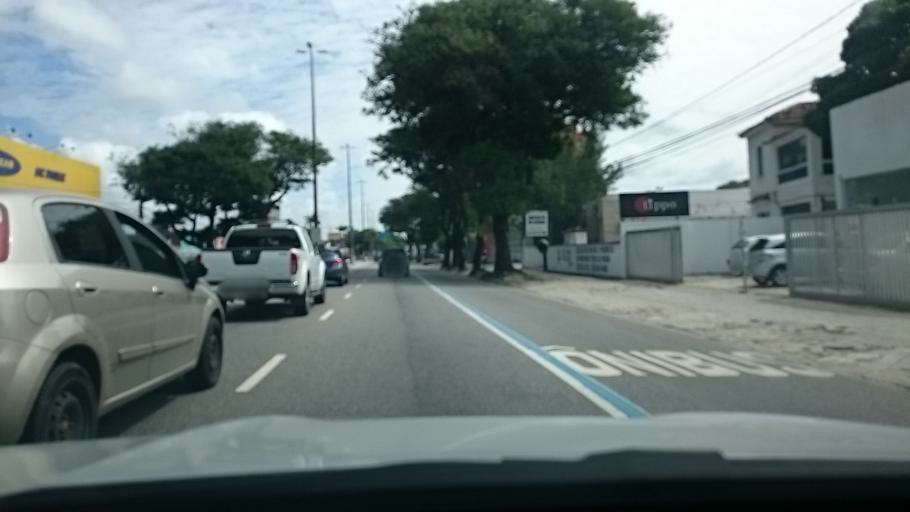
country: BR
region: Paraiba
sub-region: Joao Pessoa
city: Joao Pessoa
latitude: -7.1197
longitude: -34.8646
